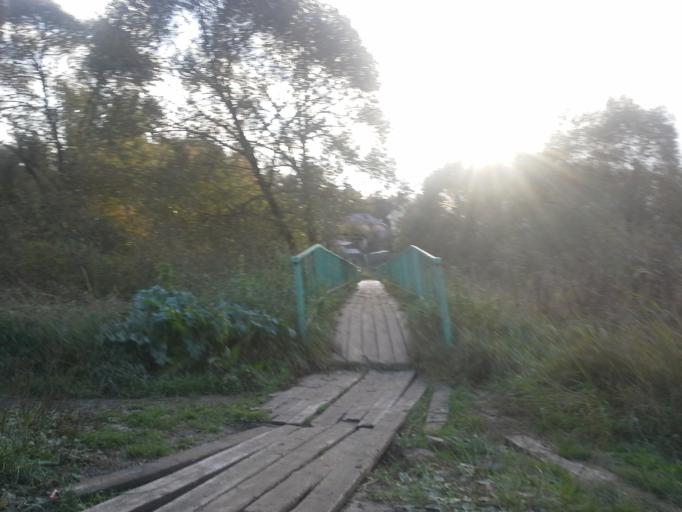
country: RU
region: Moskovskaya
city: Kommunarka
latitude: 55.5269
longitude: 37.4376
